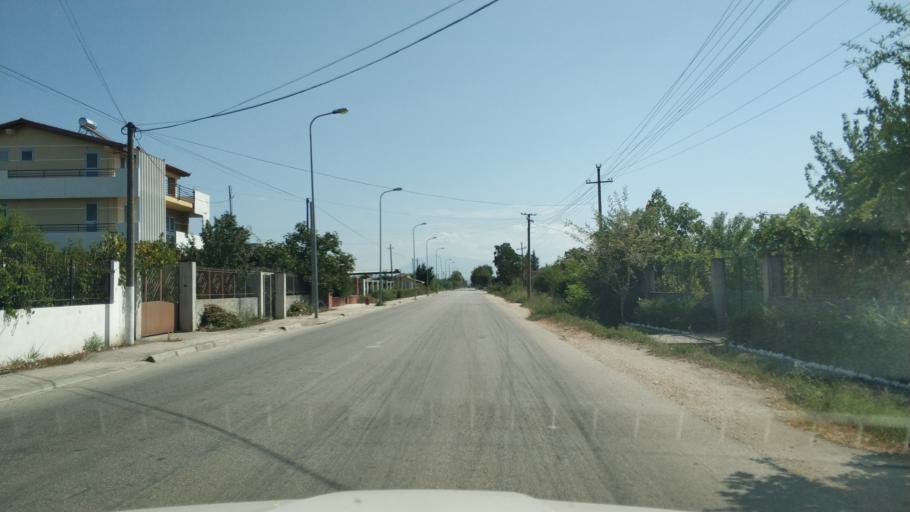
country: AL
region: Fier
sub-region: Rrethi i Lushnjes
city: Krutja e Poshtme
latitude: 40.8906
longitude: 19.6404
